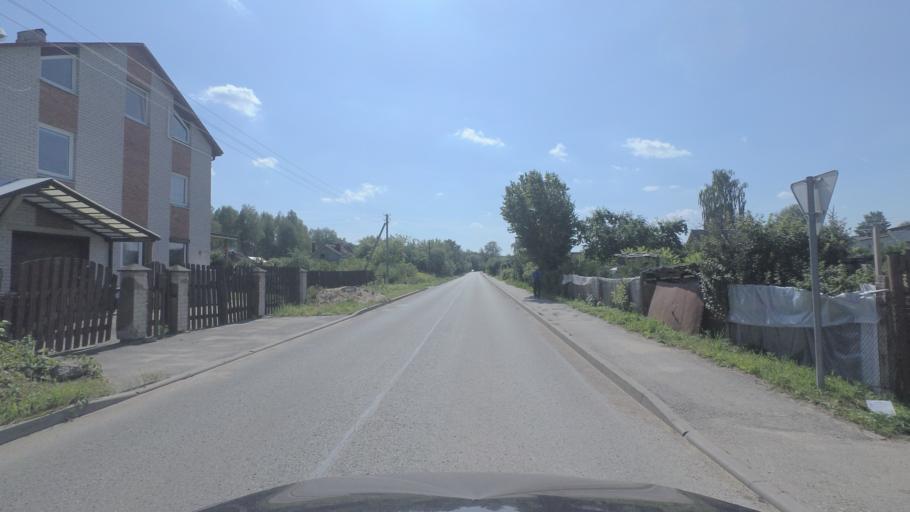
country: LT
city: Nemencine
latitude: 54.8352
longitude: 25.3697
